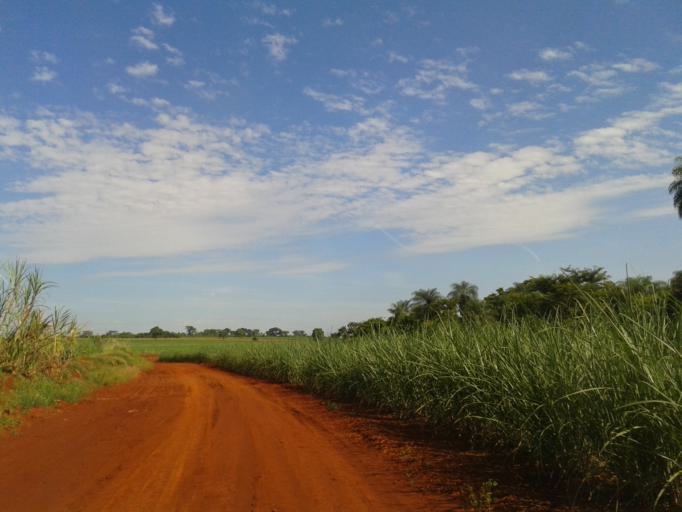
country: BR
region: Minas Gerais
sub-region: Centralina
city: Centralina
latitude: -18.6362
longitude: -49.2579
